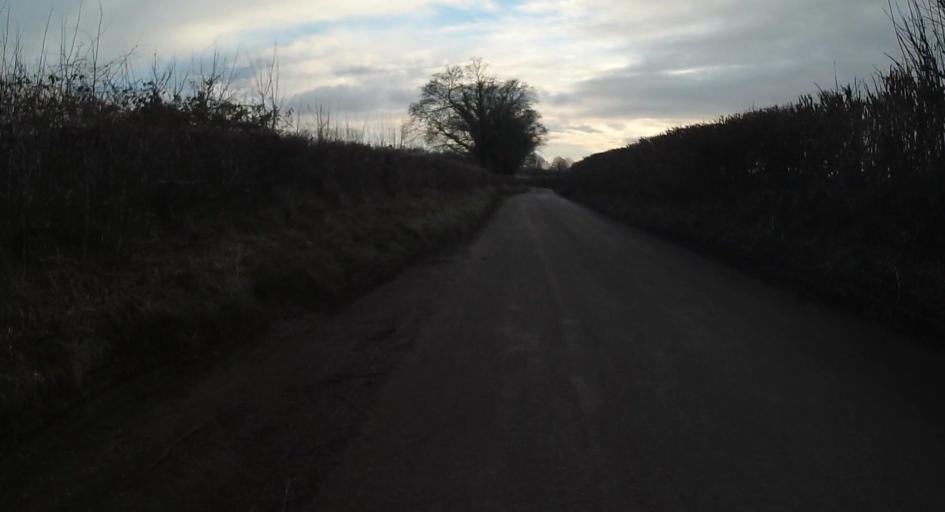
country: GB
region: England
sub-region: Hampshire
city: Swanmore
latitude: 51.0413
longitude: -1.1615
